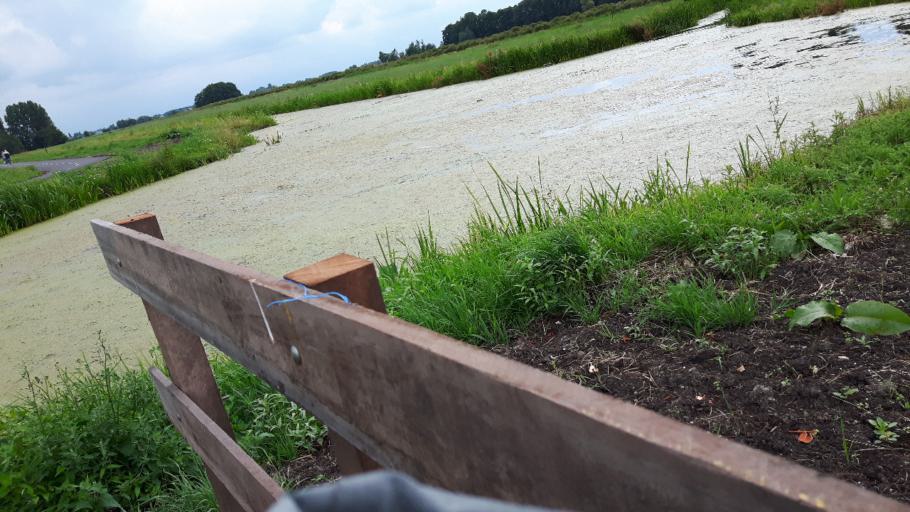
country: NL
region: South Holland
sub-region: Gemeente Vlist
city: Haastrecht
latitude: 51.9592
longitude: 4.7429
